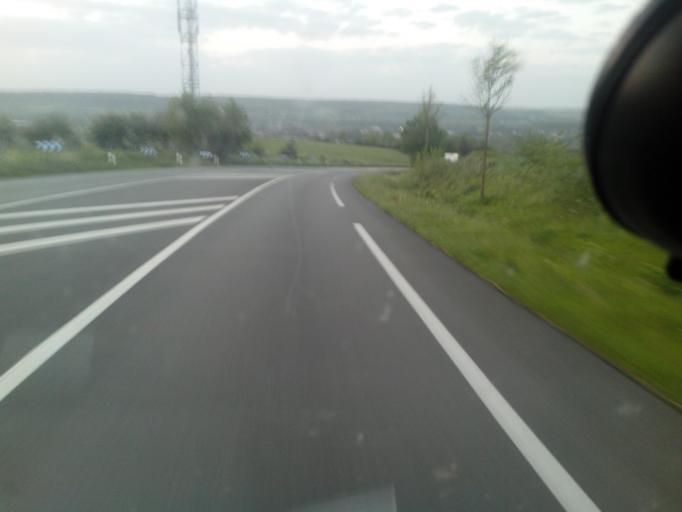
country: FR
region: Nord-Pas-de-Calais
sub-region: Departement du Pas-de-Calais
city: Hesdin
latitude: 50.3547
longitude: 2.0346
